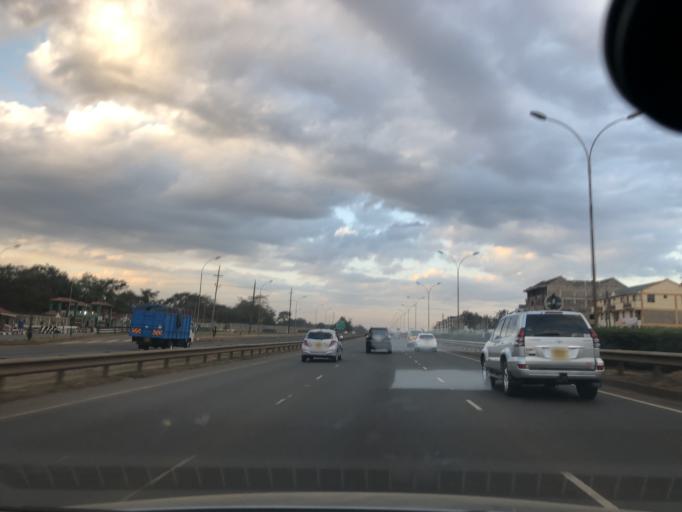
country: KE
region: Kiambu
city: Kiambu
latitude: -1.1955
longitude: 36.9246
